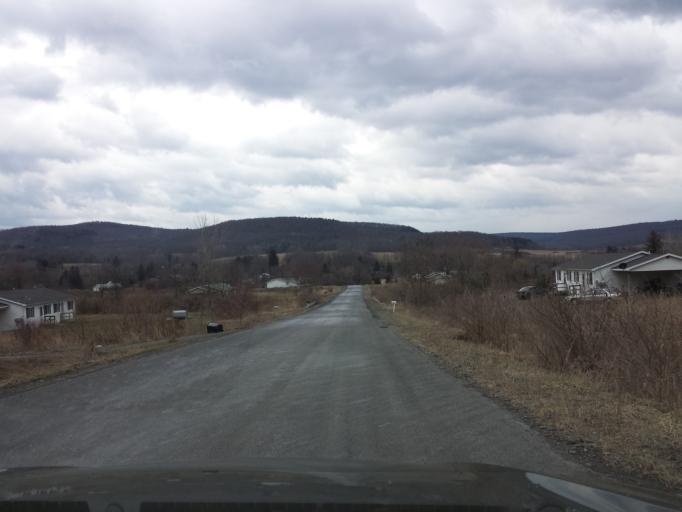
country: US
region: New York
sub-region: Tompkins County
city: Dryden
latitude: 42.3988
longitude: -76.3466
